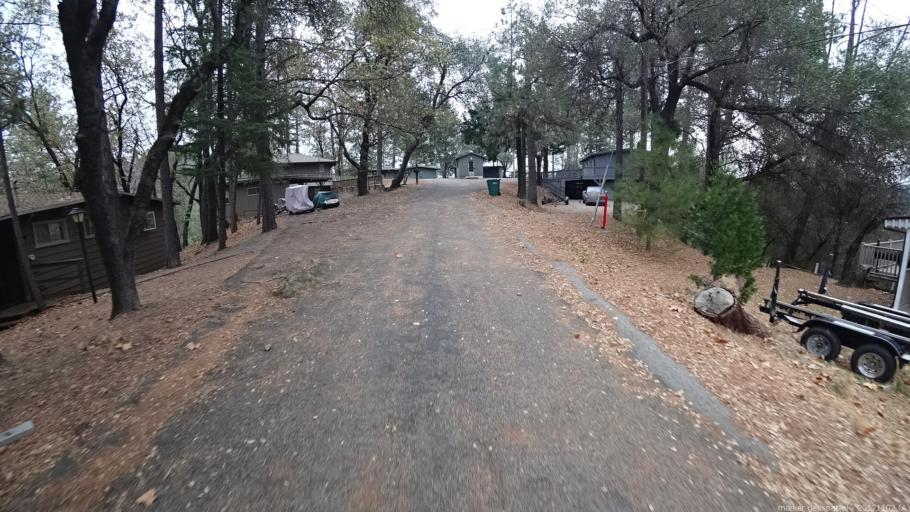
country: US
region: California
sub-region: Shasta County
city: Bella Vista
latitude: 40.7470
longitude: -122.2341
